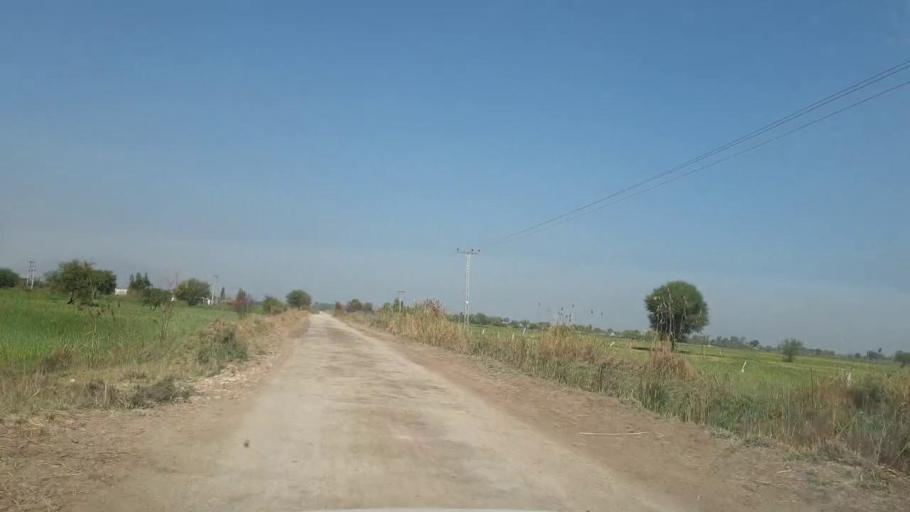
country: PK
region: Sindh
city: Pithoro
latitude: 25.5748
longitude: 69.2031
